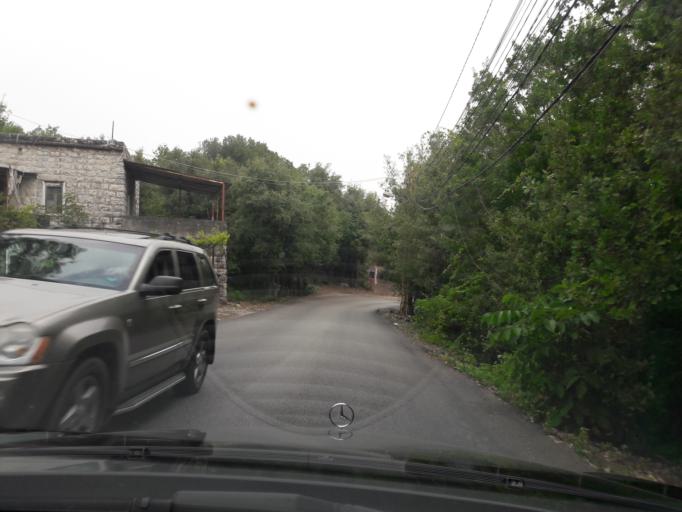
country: LB
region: Mont-Liban
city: Djounie
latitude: 33.9893
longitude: 35.6791
